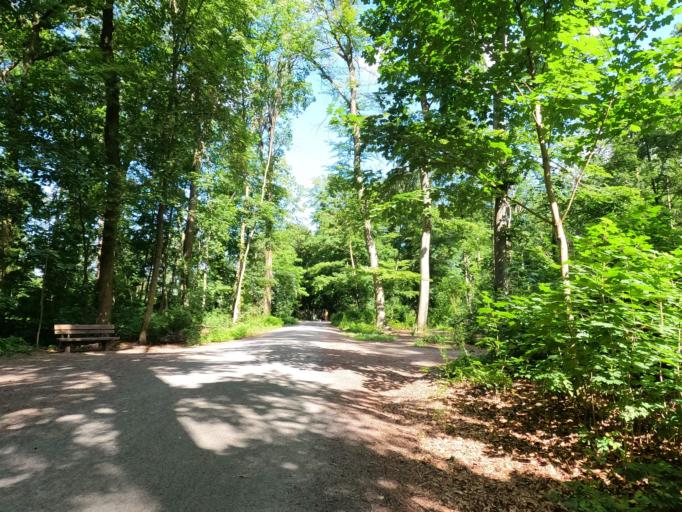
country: DE
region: Hesse
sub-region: Regierungsbezirk Darmstadt
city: Frankfurt am Main
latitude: 50.0868
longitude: 8.7128
